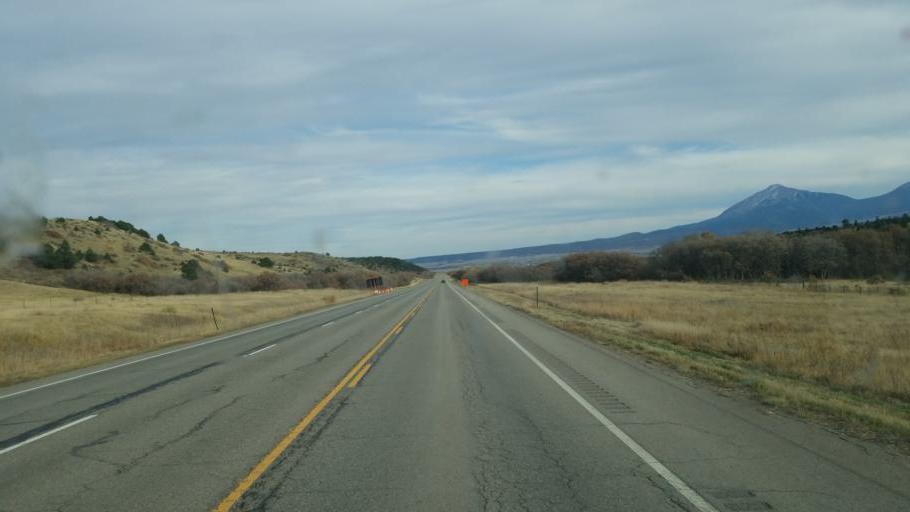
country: US
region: Colorado
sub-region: Huerfano County
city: Walsenburg
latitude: 37.5518
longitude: -105.1063
